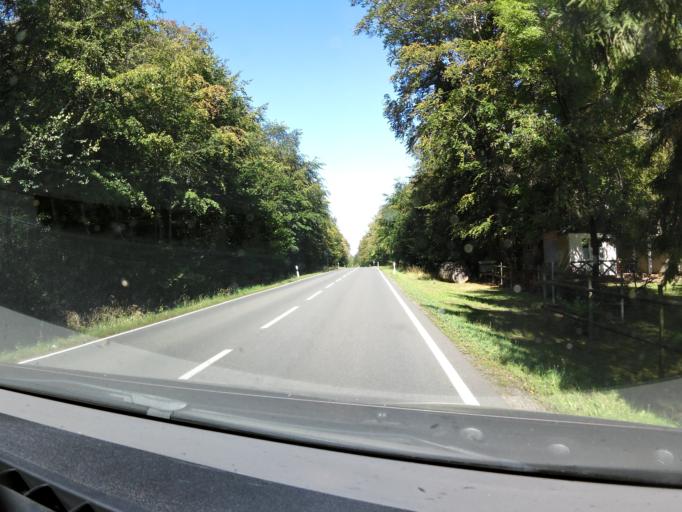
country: DE
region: Saxony-Anhalt
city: Gernrode
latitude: 51.6910
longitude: 11.1351
